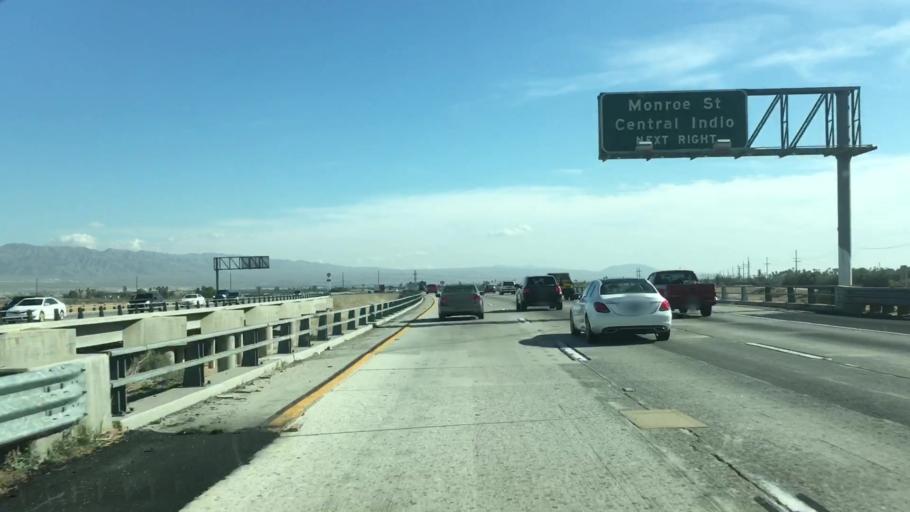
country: US
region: California
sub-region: Riverside County
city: Indio
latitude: 33.7391
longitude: -116.2500
